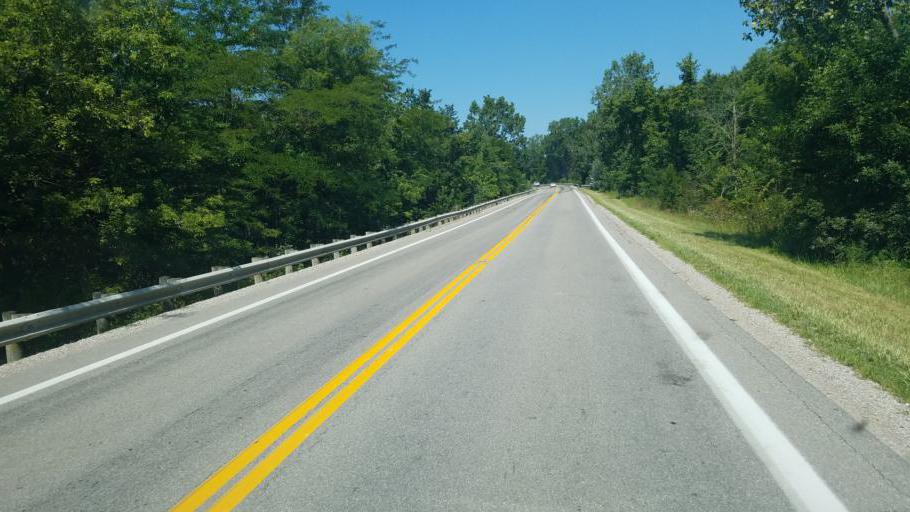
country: US
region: Ohio
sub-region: Delaware County
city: Ashley
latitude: 40.4325
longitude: -83.0466
